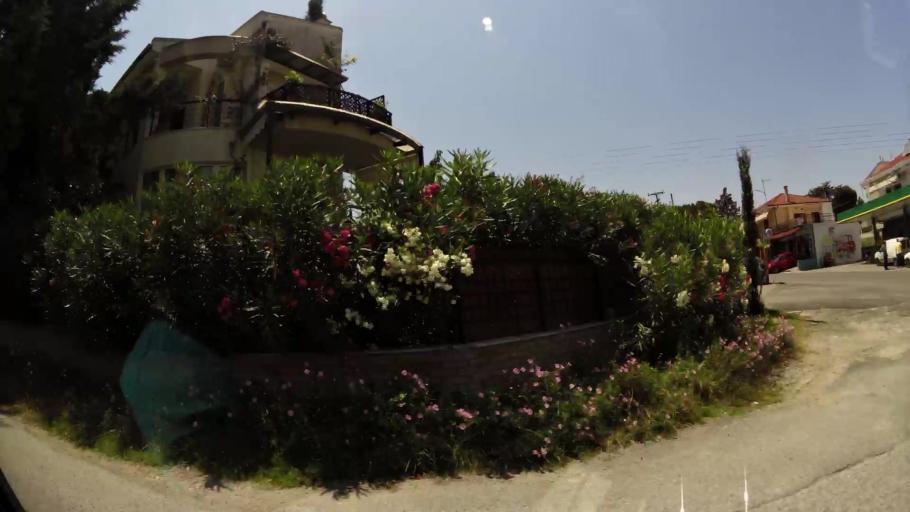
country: GR
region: Central Macedonia
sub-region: Nomos Thessalonikis
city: Trilofos
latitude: 40.4722
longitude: 22.9730
